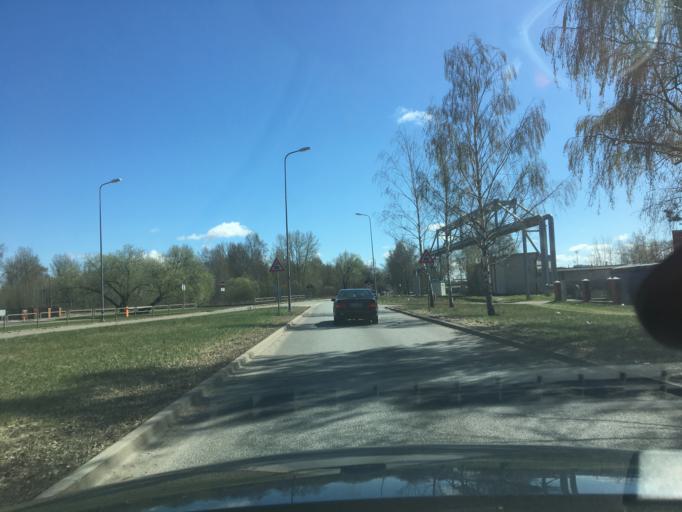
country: LV
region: Kekava
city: Balozi
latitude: 56.9196
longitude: 24.1945
